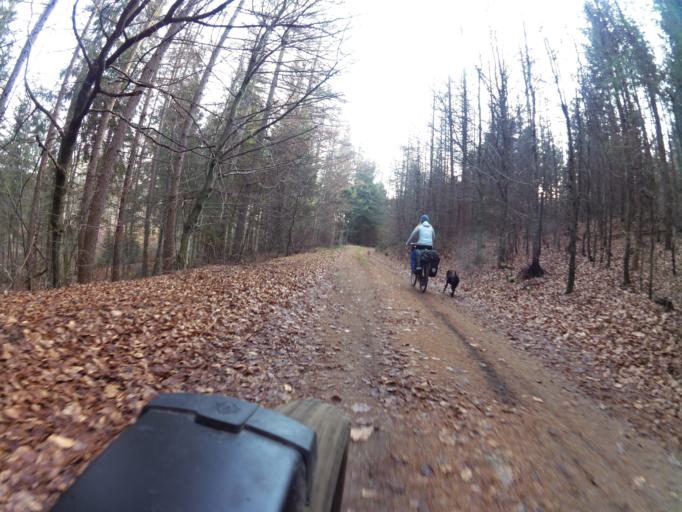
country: PL
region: West Pomeranian Voivodeship
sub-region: Powiat koszalinski
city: Polanow
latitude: 54.1674
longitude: 16.7281
